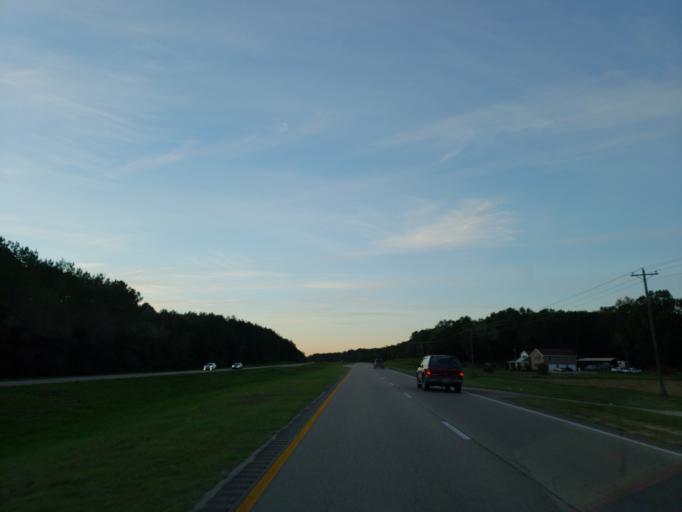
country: US
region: Mississippi
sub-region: Wayne County
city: Belmont
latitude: 31.5969
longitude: -88.5540
